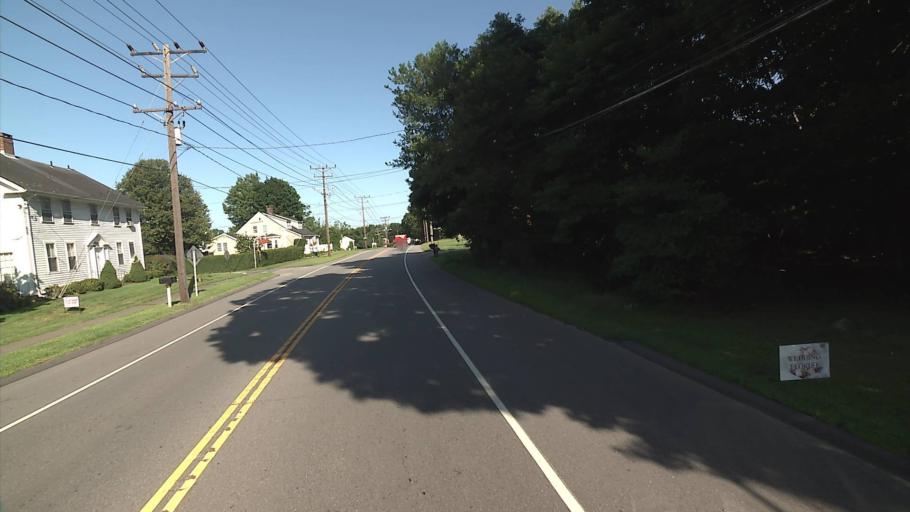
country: US
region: Connecticut
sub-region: Middlesex County
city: Westbrook Center
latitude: 41.2819
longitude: -72.4383
